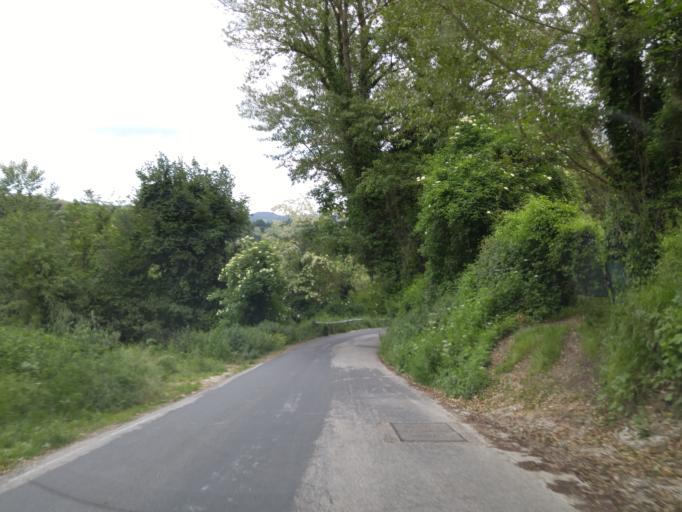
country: IT
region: The Marches
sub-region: Provincia di Pesaro e Urbino
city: Urbino
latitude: 43.7194
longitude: 12.6296
